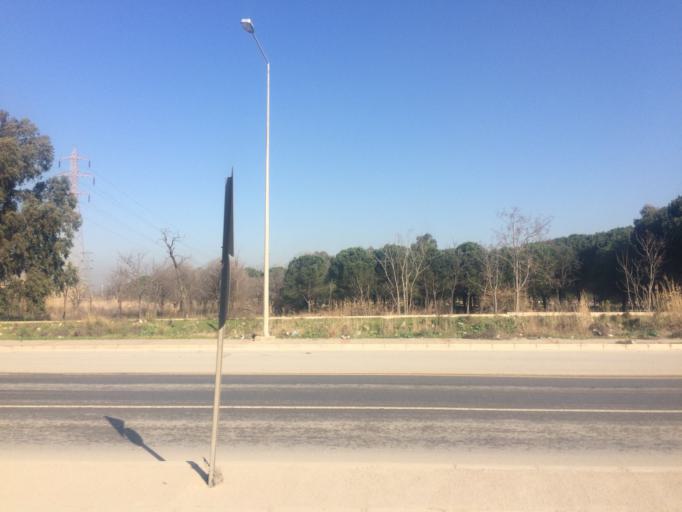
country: TR
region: Izmir
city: Menemen
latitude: 38.5183
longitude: 27.0331
